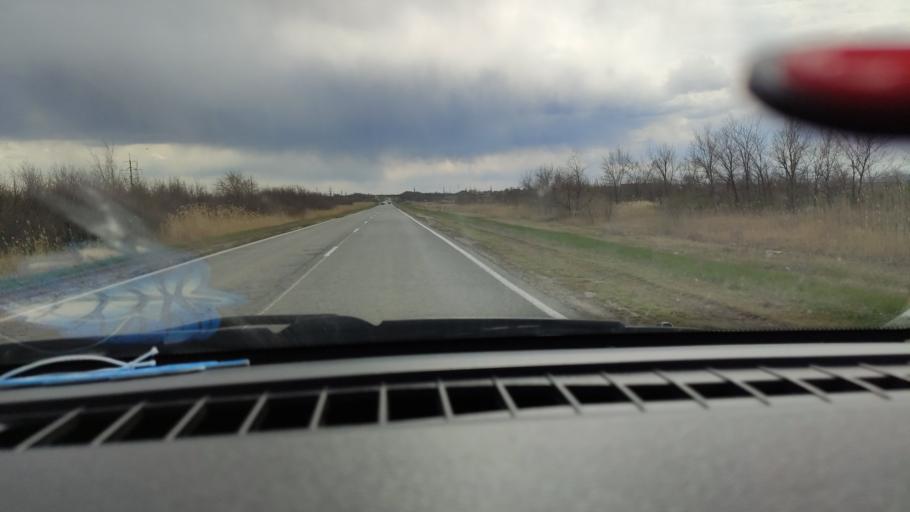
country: RU
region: Saratov
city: Privolzhskiy
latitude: 51.3049
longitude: 46.0059
